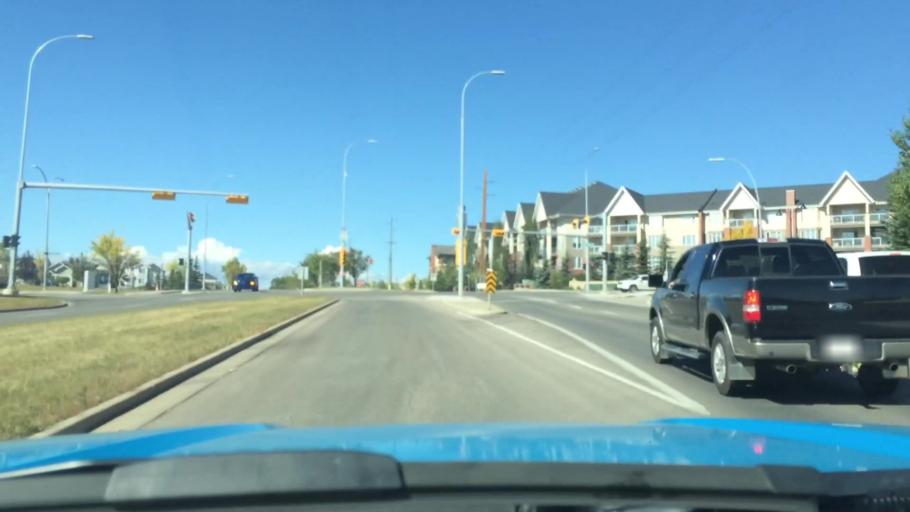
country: CA
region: Alberta
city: Calgary
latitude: 50.9066
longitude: -114.1045
